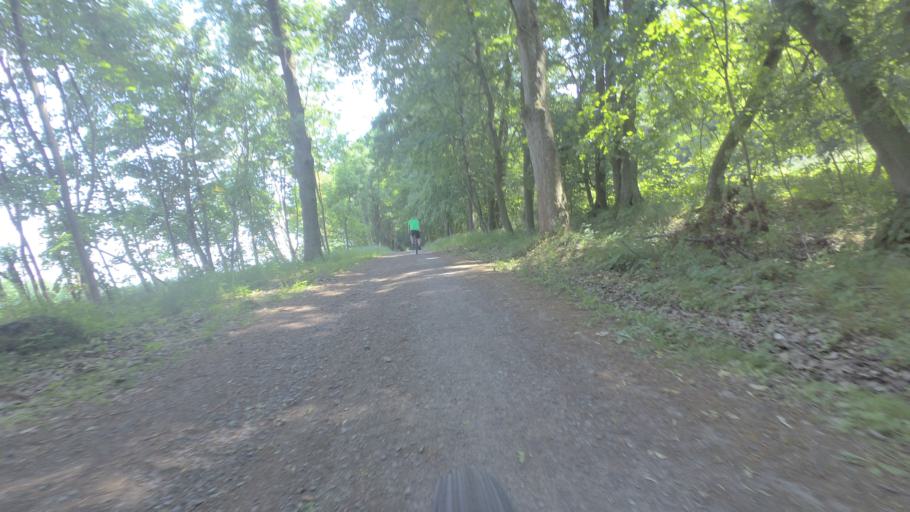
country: DE
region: Saxony-Anhalt
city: Ballenstedt
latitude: 51.7233
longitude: 11.2022
